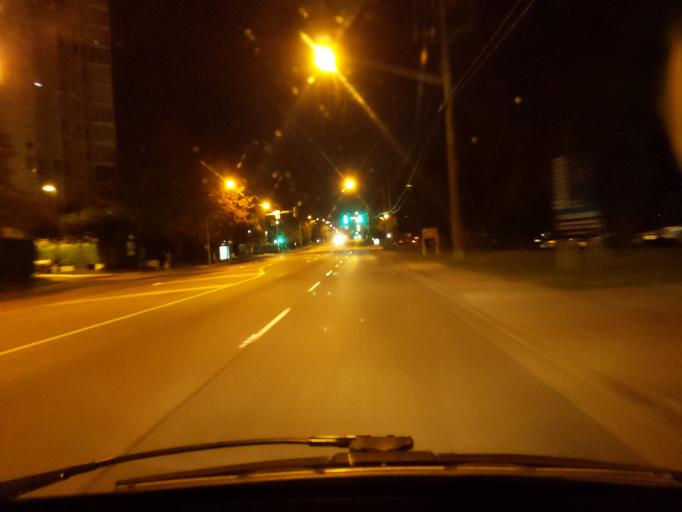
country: CA
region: British Columbia
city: Surrey
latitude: 49.1916
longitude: -122.8109
